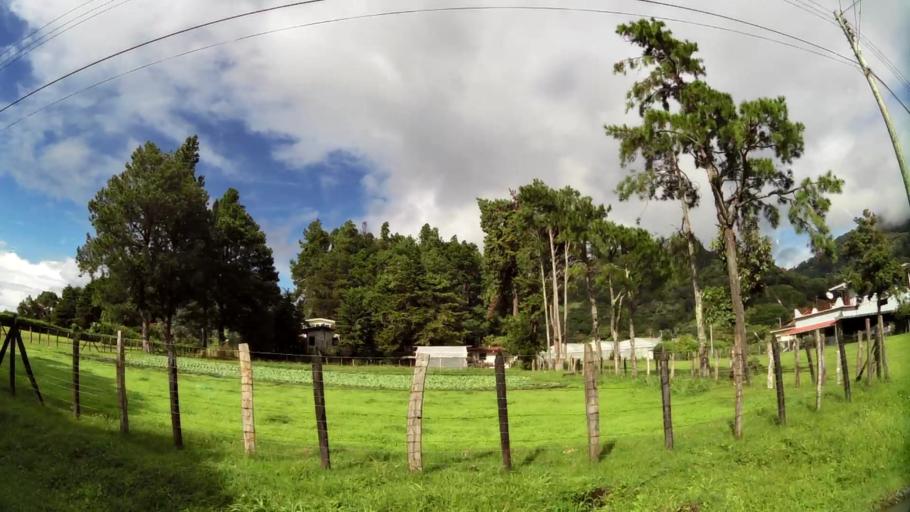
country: PA
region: Chiriqui
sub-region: Distrito Boquete
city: Boquete
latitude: 8.7980
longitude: -82.4323
